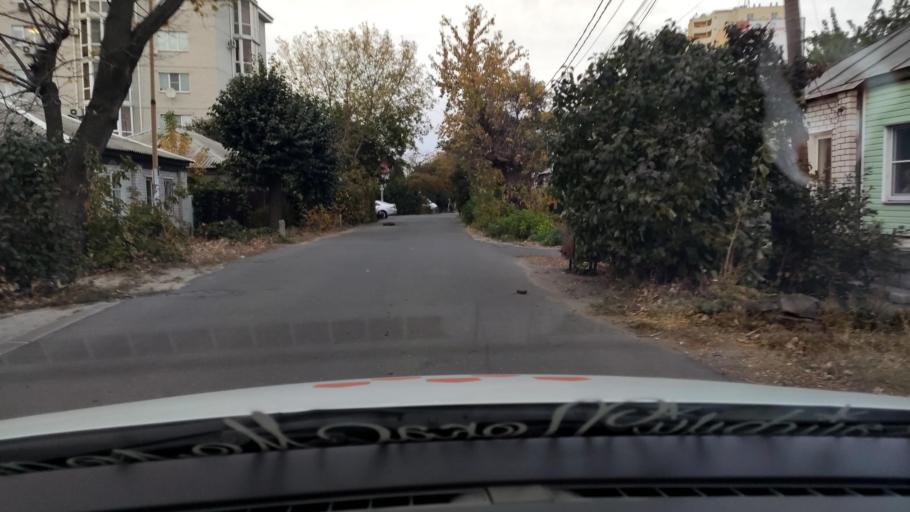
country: RU
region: Voronezj
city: Voronezh
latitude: 51.6878
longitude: 39.2171
